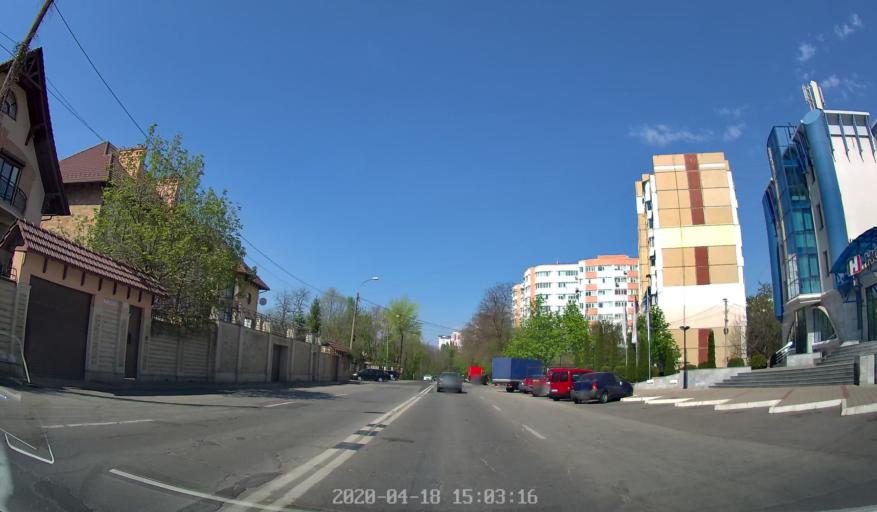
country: MD
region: Chisinau
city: Chisinau
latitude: 47.0376
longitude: 28.8790
